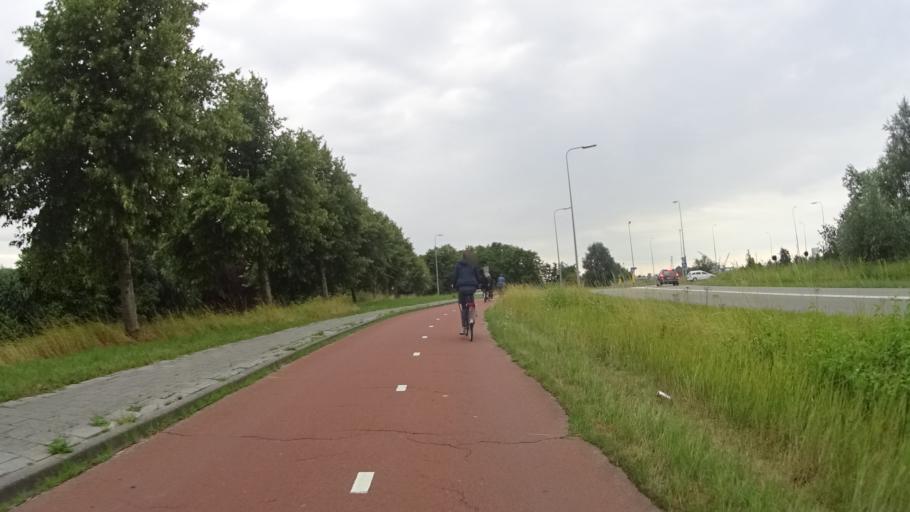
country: NL
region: Groningen
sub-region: Gemeente Groningen
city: Oosterpark
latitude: 53.2269
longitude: 6.5942
